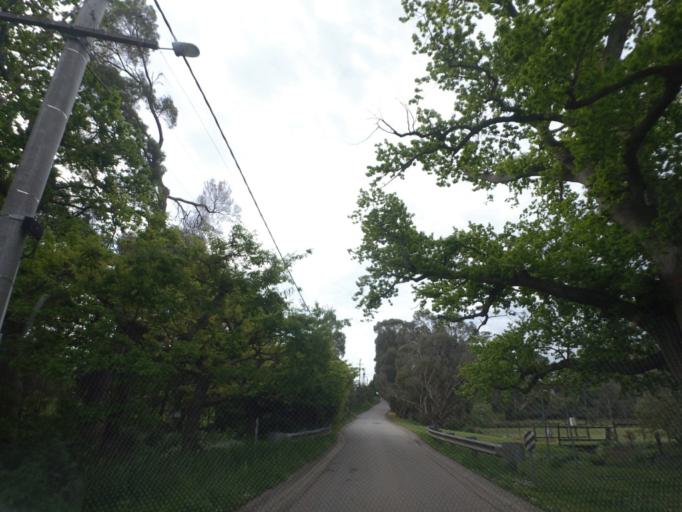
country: AU
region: Victoria
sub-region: Knox
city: The Basin
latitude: -37.8551
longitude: 145.3227
